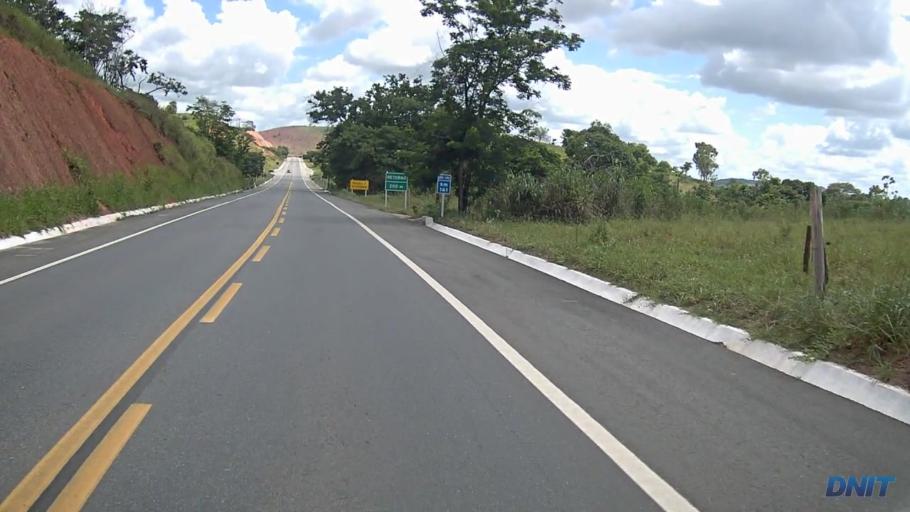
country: BR
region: Minas Gerais
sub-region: Governador Valadares
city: Governador Valadares
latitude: -18.9041
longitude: -42.0033
